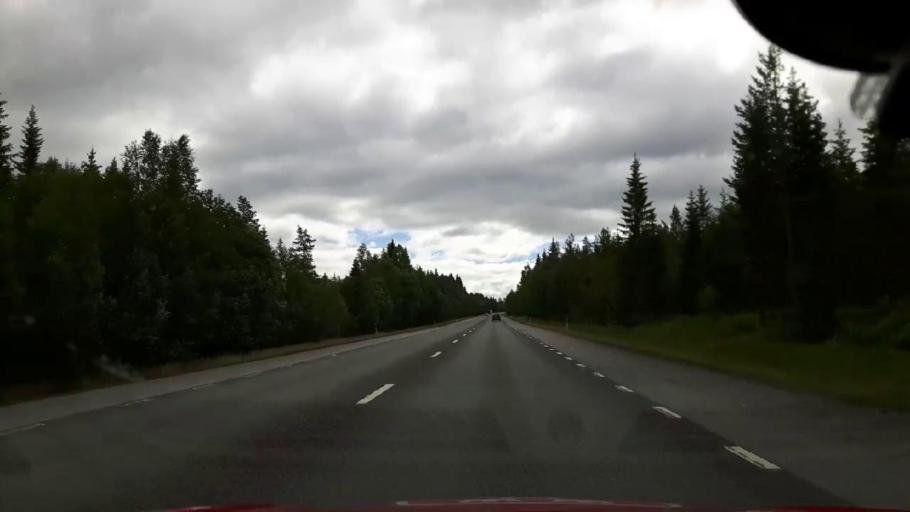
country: SE
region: Jaemtland
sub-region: Braecke Kommun
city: Braecke
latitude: 62.7071
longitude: 15.4915
